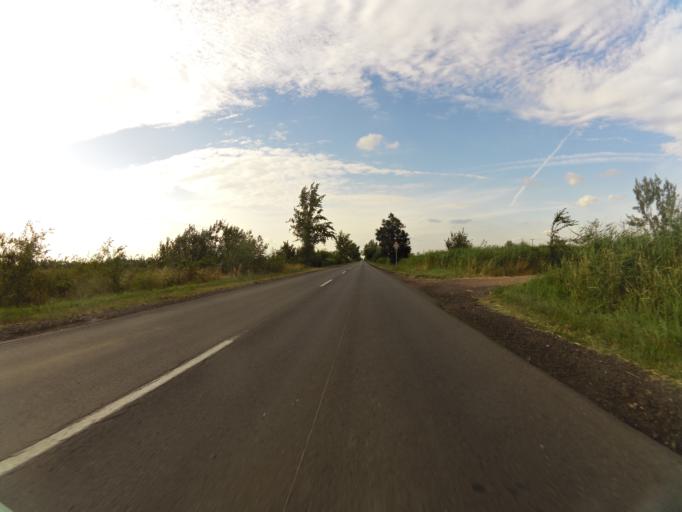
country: HU
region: Csongrad
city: Sandorfalva
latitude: 46.3158
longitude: 20.1297
